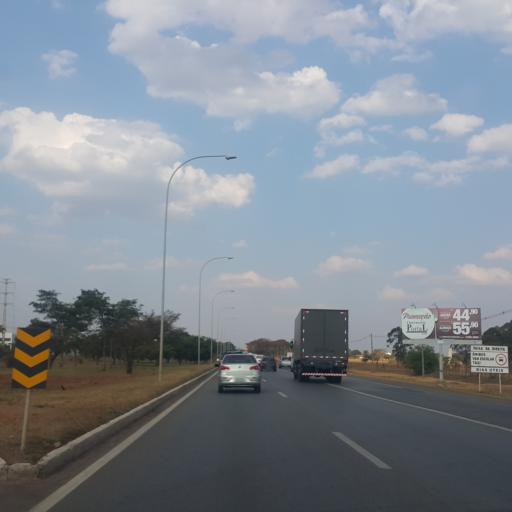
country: BR
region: Federal District
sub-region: Brasilia
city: Brasilia
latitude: -15.8748
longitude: -48.0372
